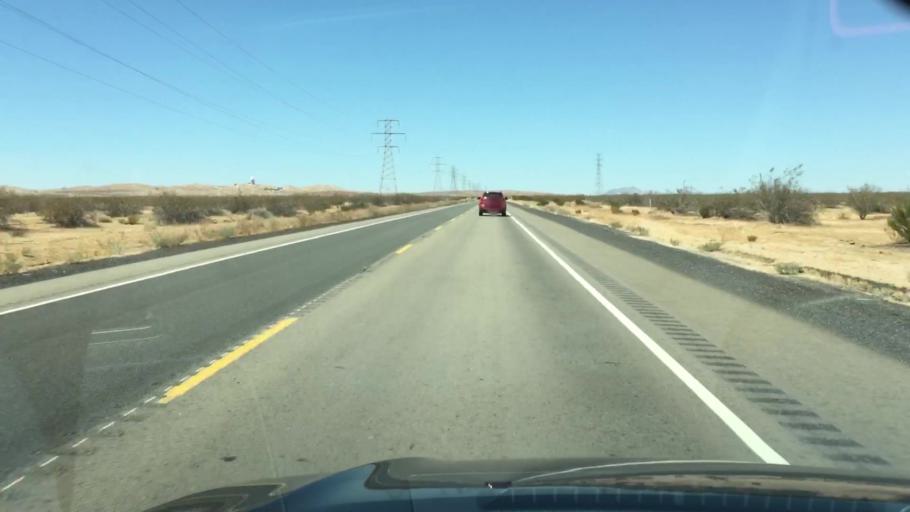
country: US
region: California
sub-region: Kern County
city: Boron
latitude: 35.0376
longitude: -117.5541
